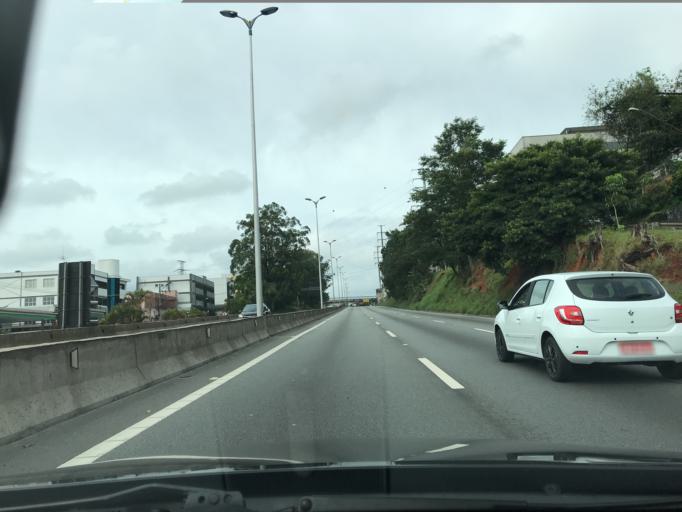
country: BR
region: Sao Paulo
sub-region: Embu
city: Embu
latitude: -23.5979
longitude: -46.8426
